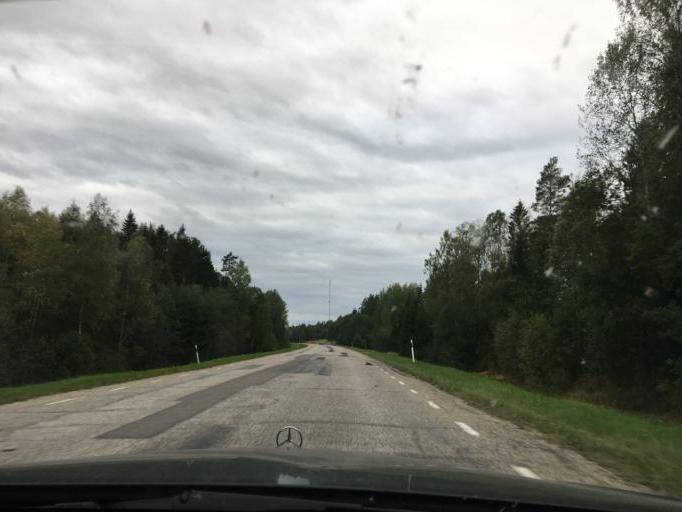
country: LV
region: Aluksnes Rajons
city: Aluksne
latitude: 57.5960
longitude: 27.0971
